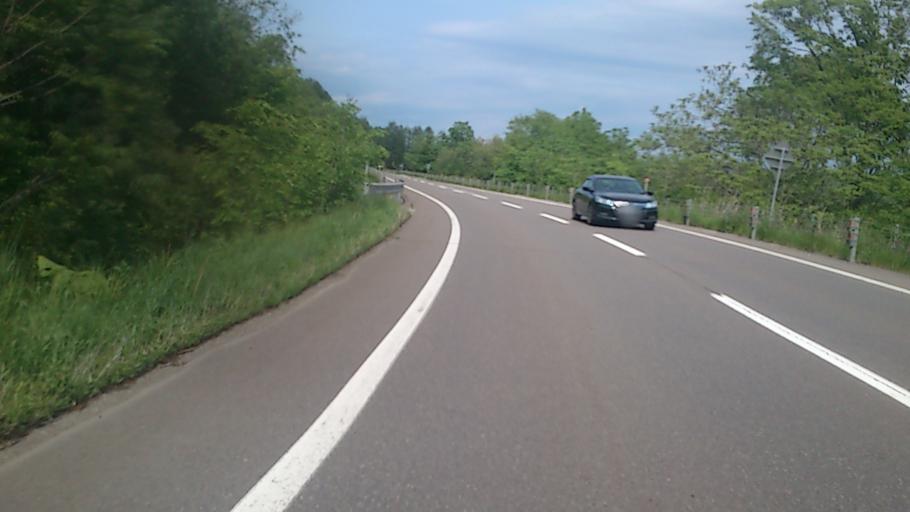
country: JP
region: Hokkaido
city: Otofuke
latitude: 43.2871
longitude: 143.6537
